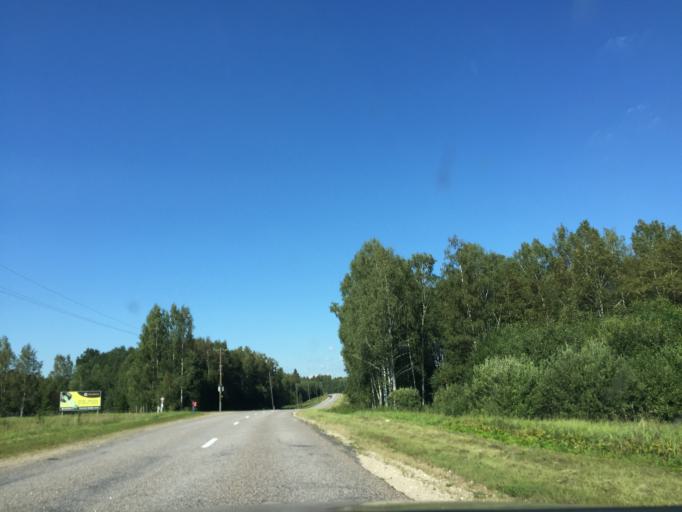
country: LV
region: Limbazu Rajons
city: Limbazi
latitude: 57.4684
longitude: 24.7120
